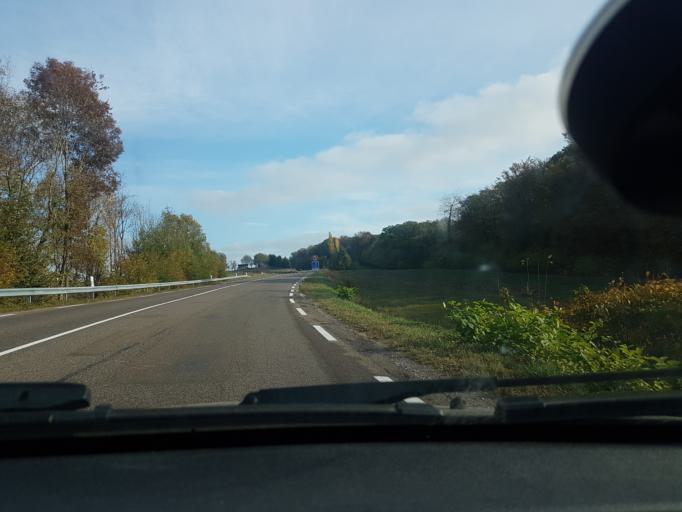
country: FR
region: Franche-Comte
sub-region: Departement de la Haute-Saone
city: Chalonvillars
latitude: 47.6499
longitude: 6.7669
